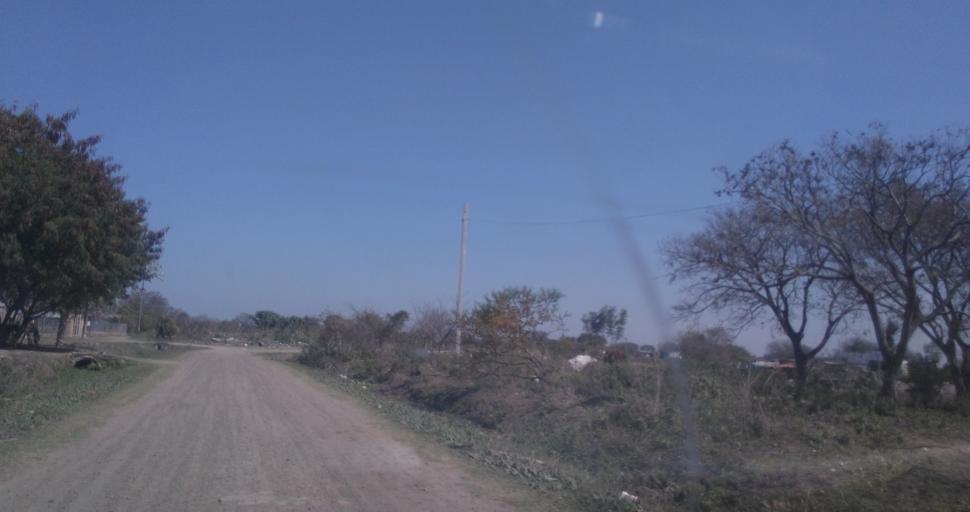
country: AR
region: Chaco
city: Fontana
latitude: -27.4332
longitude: -59.0295
